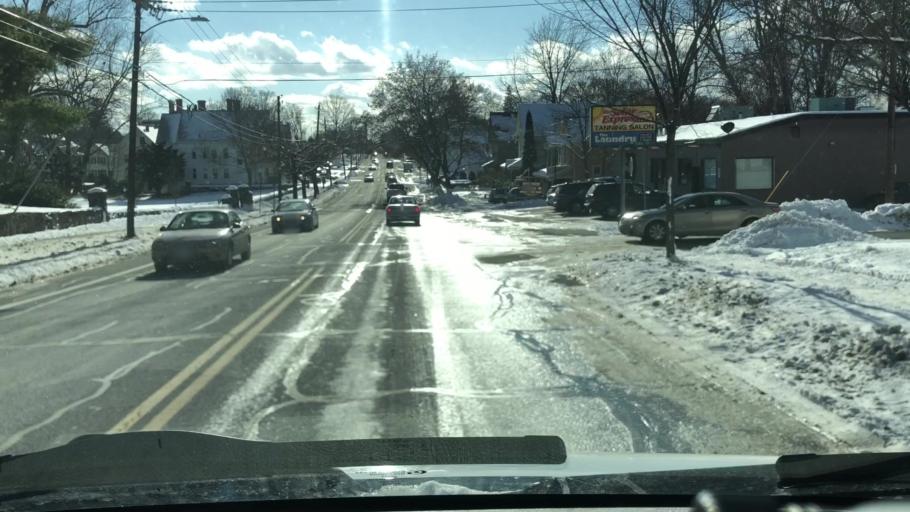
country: US
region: Massachusetts
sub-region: Franklin County
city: Greenfield
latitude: 42.5947
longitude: -72.5976
